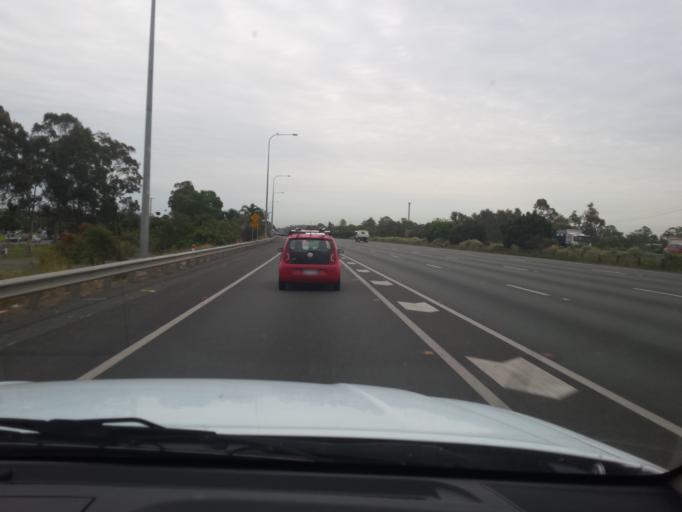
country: AU
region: Queensland
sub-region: Gold Coast
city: Oxenford
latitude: -27.8811
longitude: 153.3151
